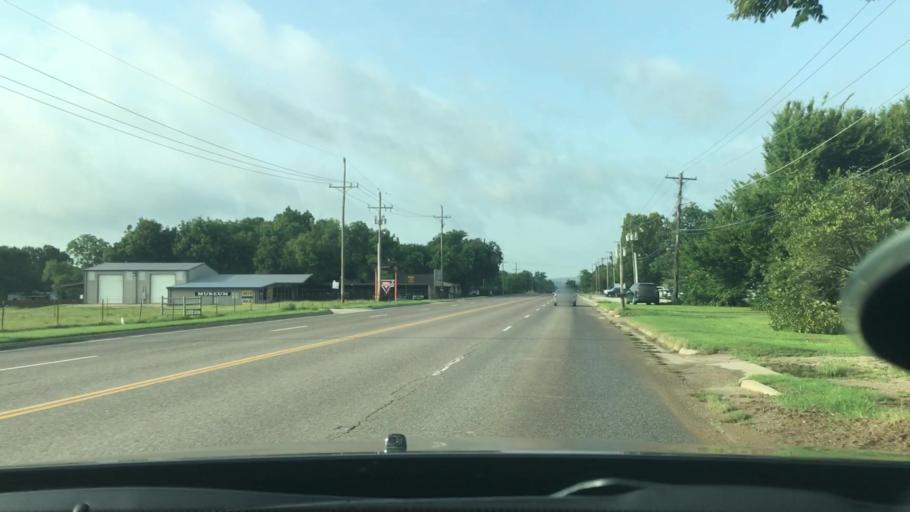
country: US
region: Oklahoma
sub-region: Murray County
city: Davis
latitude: 34.4825
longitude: -97.1308
